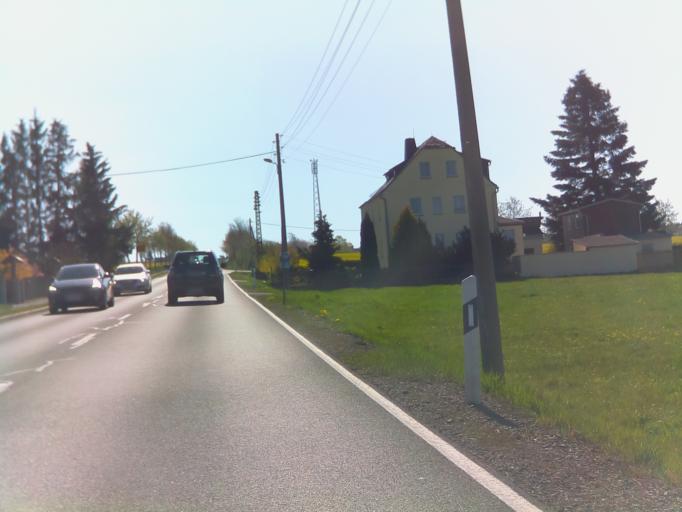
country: DE
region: Saxony
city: Mehltheuer
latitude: 50.5469
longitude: 12.0248
